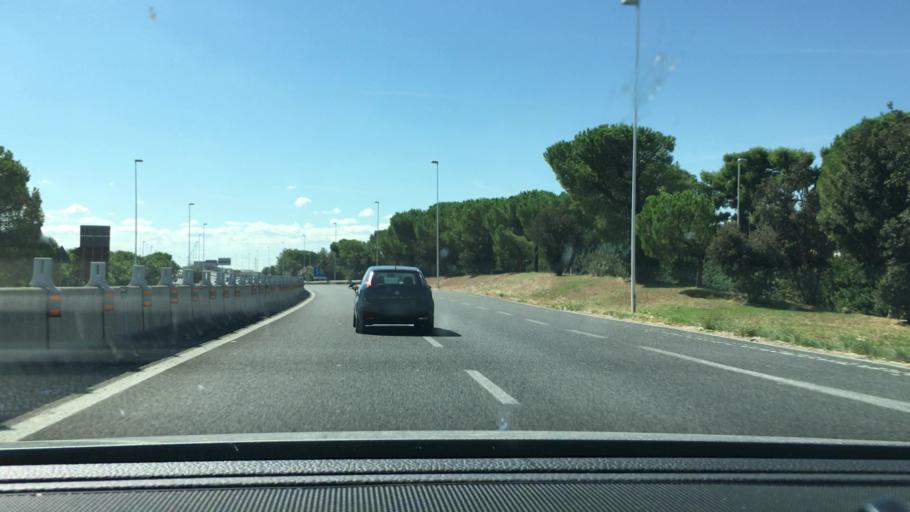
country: IT
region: Apulia
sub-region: Provincia di Bari
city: Bitritto
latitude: 41.0795
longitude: 16.8337
